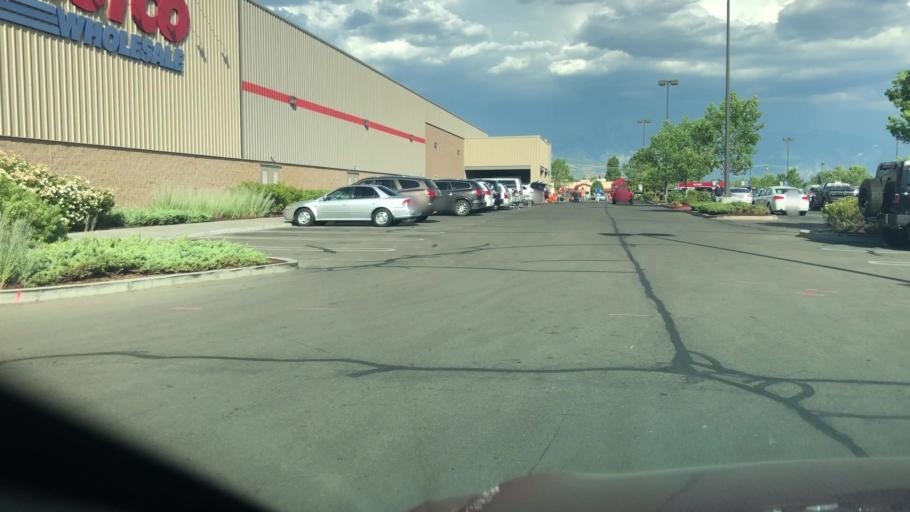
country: US
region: Utah
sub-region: Utah County
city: Lehi
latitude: 40.3896
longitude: -111.8243
